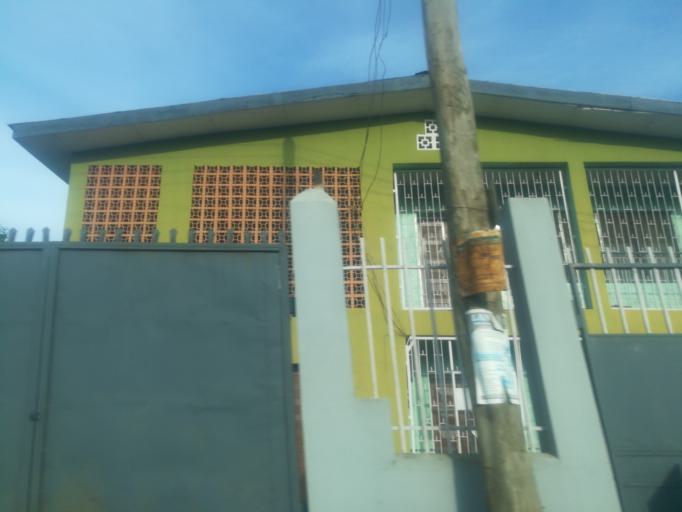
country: NG
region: Oyo
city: Ibadan
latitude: 7.3378
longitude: 3.8901
